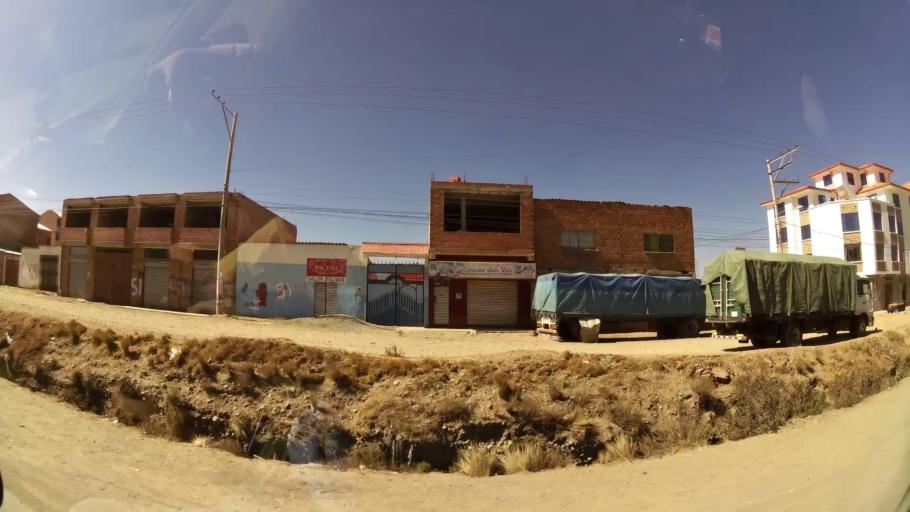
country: BO
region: La Paz
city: La Paz
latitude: -16.5520
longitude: -68.2068
